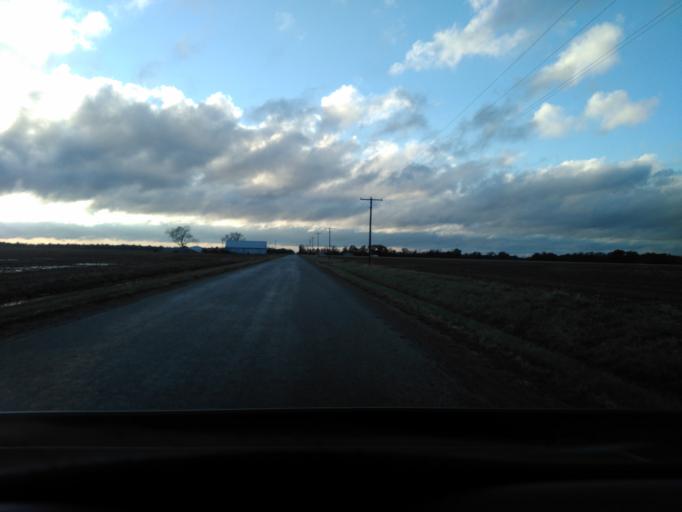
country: US
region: Illinois
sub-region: Effingham County
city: Altamont
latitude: 38.9574
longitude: -88.7386
